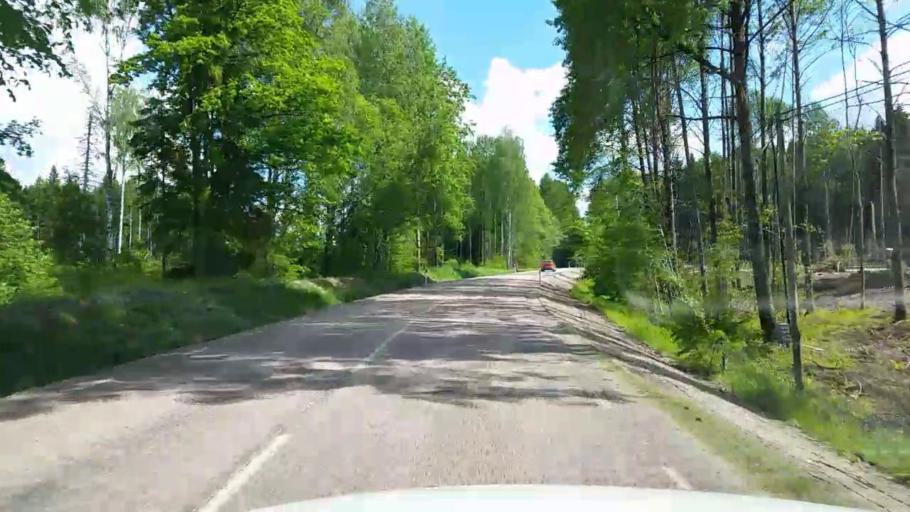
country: SE
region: Vaestmanland
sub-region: Skinnskattebergs Kommun
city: Skinnskatteberg
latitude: 59.7725
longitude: 15.8405
